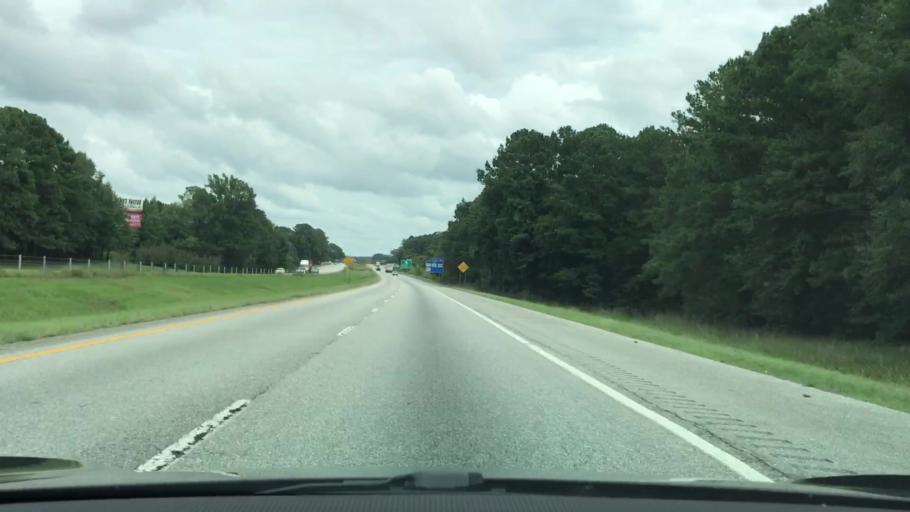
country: US
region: Alabama
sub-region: Chambers County
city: Valley
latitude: 32.8404
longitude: -85.1938
